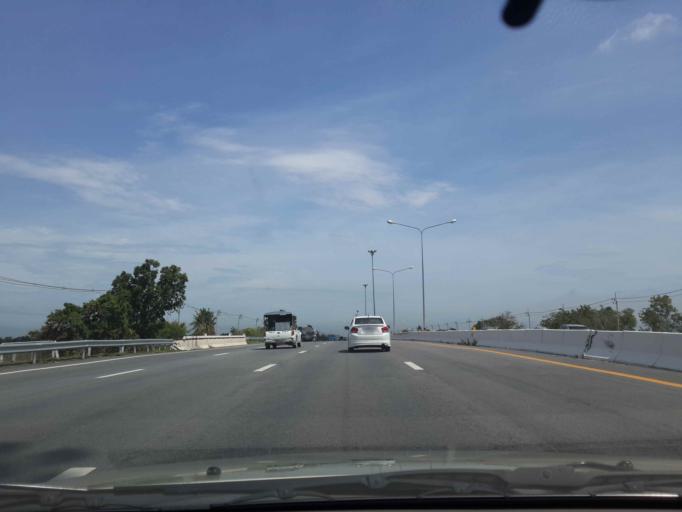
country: TH
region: Samut Prakan
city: Ban Khlong Bang Sao Thong
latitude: 13.6260
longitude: 100.9123
